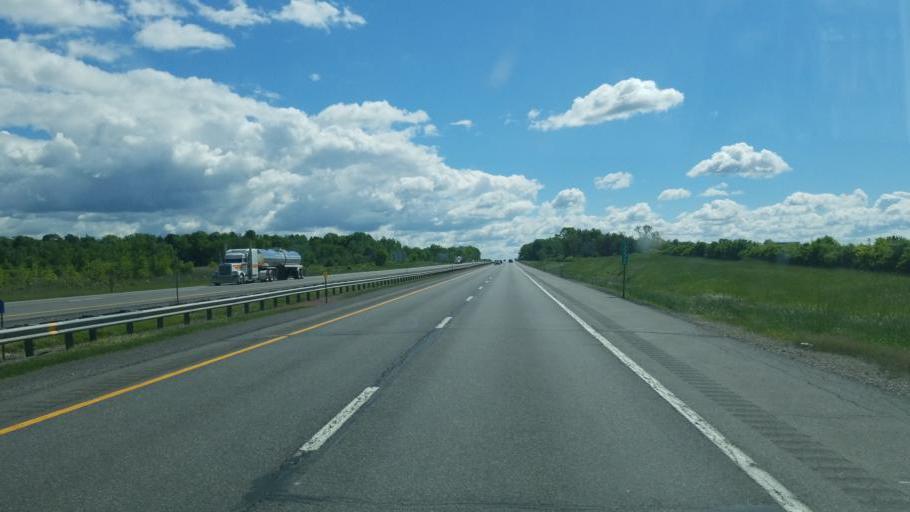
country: US
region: New York
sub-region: Oneida County
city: Vernon
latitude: 43.1253
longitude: -75.5691
